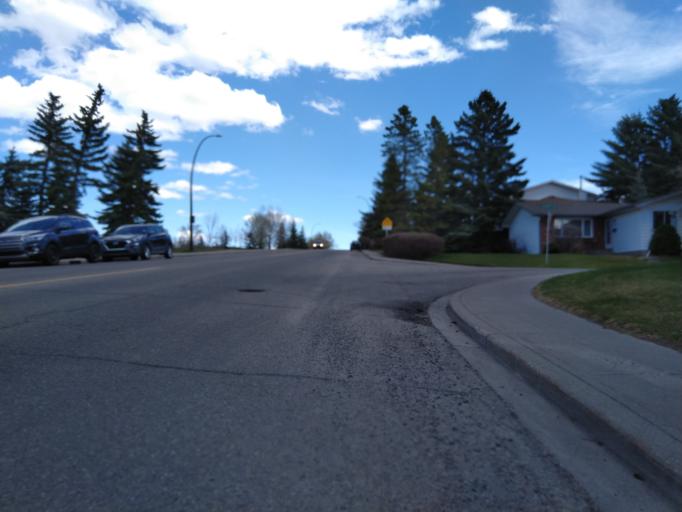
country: CA
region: Alberta
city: Calgary
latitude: 51.0124
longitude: -114.1583
